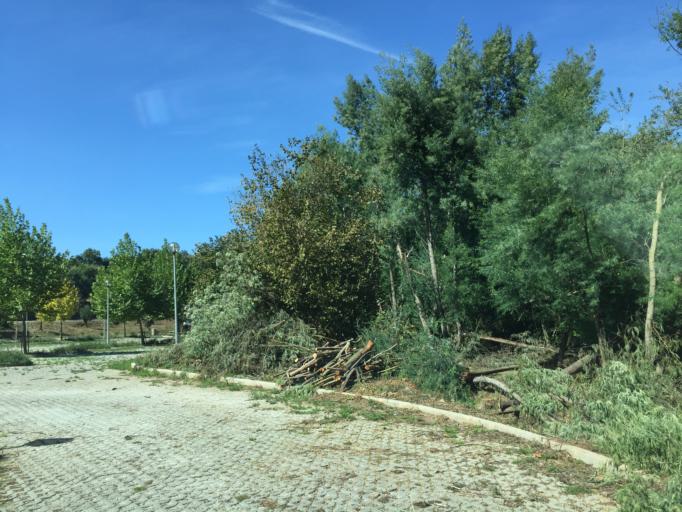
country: PT
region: Portalegre
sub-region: Marvao
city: Marvao
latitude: 39.3841
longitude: -7.3833
